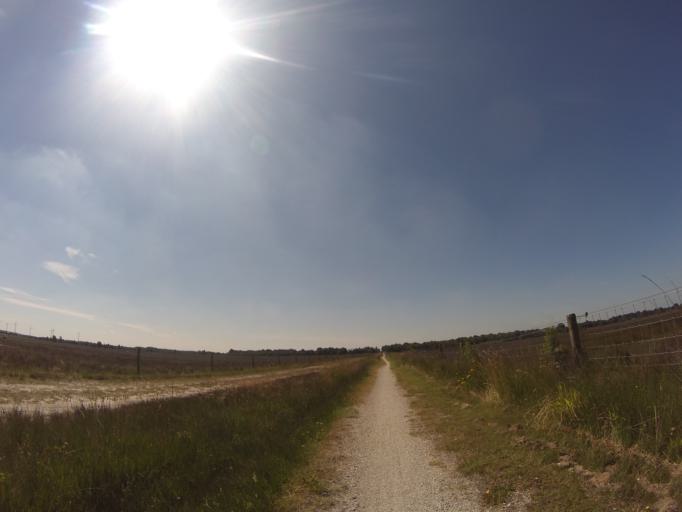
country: DE
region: Lower Saxony
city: Twist
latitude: 52.6762
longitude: 7.0233
